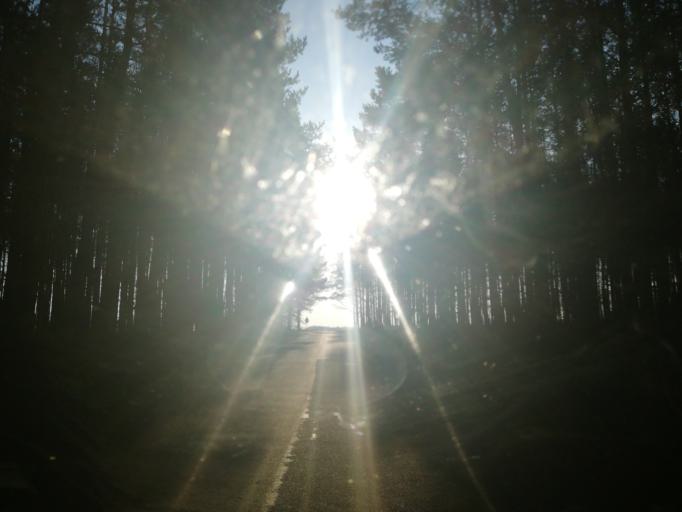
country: DE
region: Brandenburg
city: Drahnsdorf
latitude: 51.8926
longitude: 13.5869
